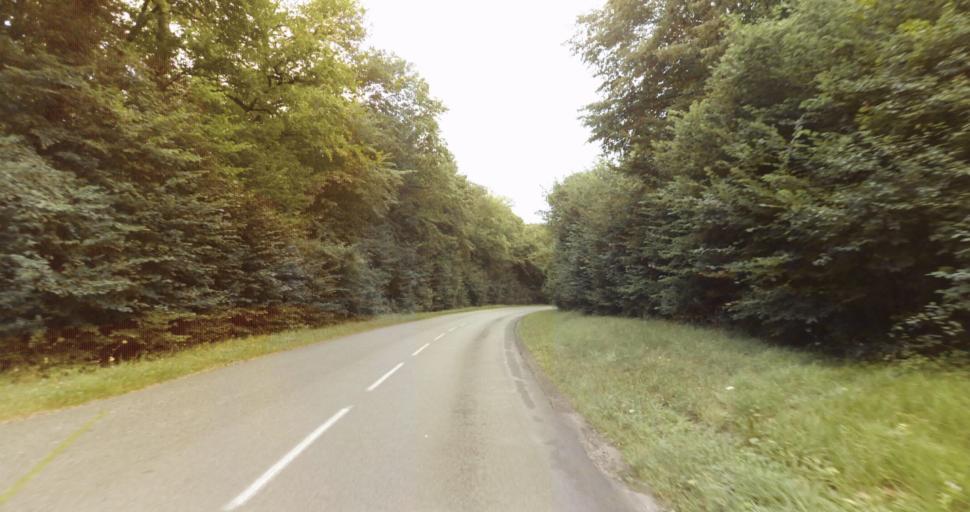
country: FR
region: Haute-Normandie
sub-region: Departement de l'Eure
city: Croth
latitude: 48.8668
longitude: 1.3813
